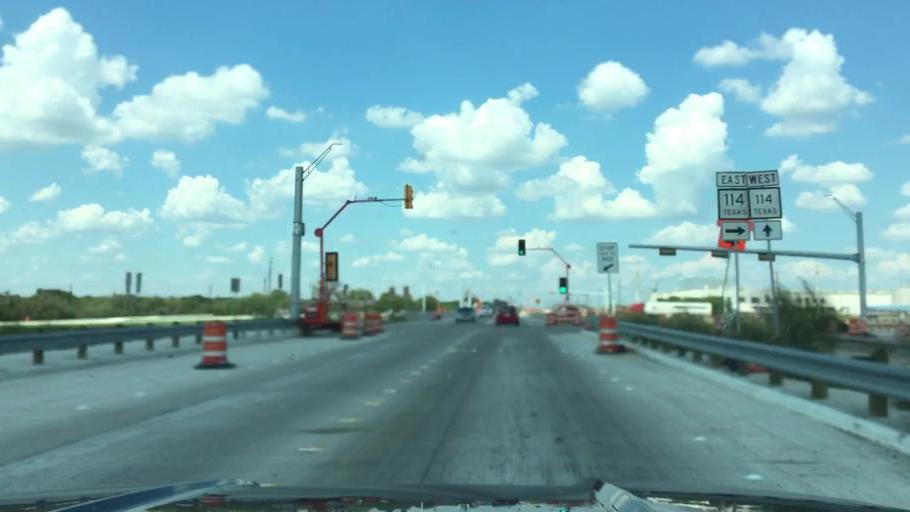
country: US
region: Texas
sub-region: Denton County
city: Justin
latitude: 33.0280
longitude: -97.3100
